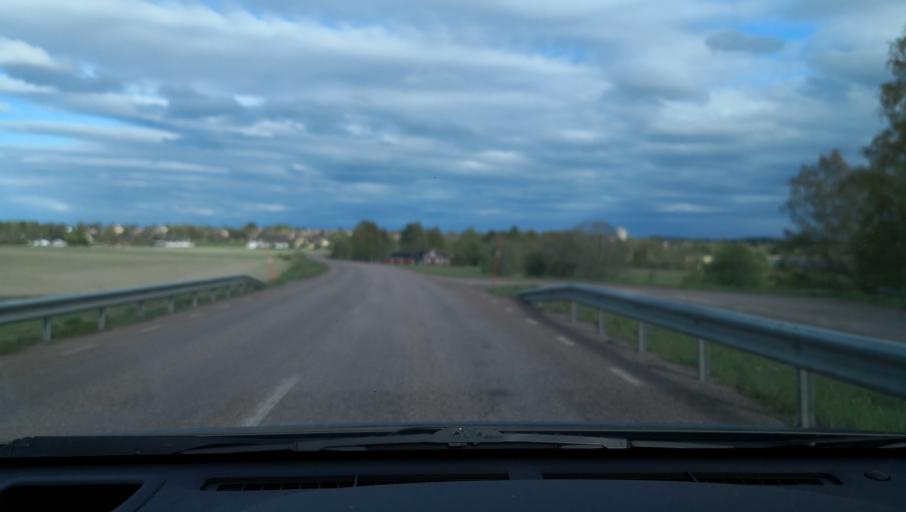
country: SE
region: Dalarna
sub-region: Hedemora Kommun
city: Hedemora
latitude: 60.2823
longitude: 15.9529
